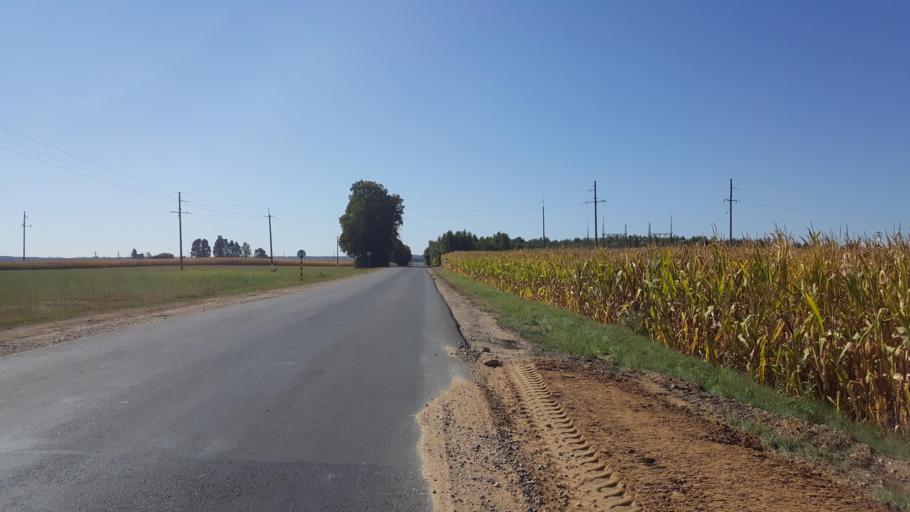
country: BY
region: Brest
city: Charnawchytsy
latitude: 52.2874
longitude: 23.6045
